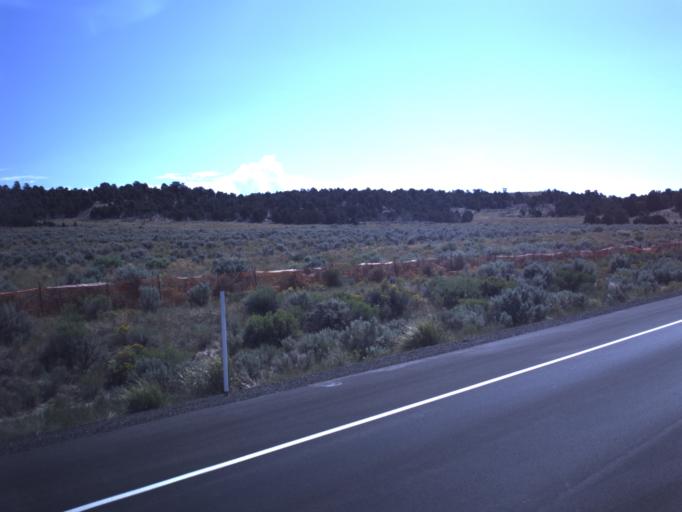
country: US
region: Utah
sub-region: Utah County
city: Genola
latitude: 39.9636
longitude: -112.2499
